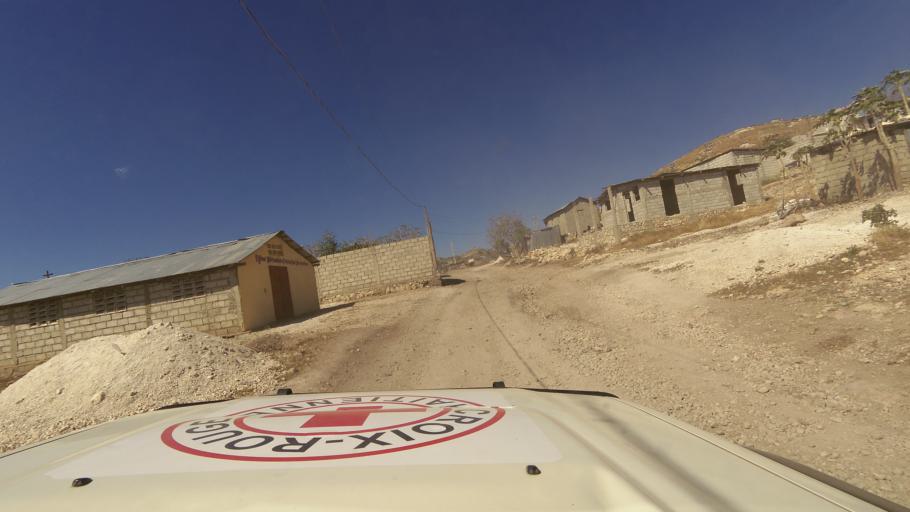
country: HT
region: Ouest
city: Croix des Bouquets
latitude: 18.6623
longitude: -72.2651
